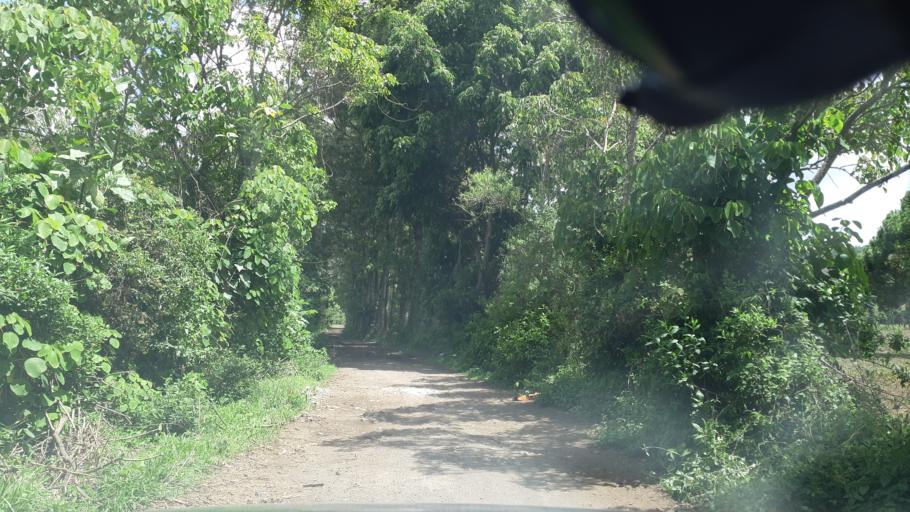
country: GT
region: Chimaltenango
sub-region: Municipio de Chimaltenango
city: Chimaltenango
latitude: 14.6550
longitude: -90.8487
